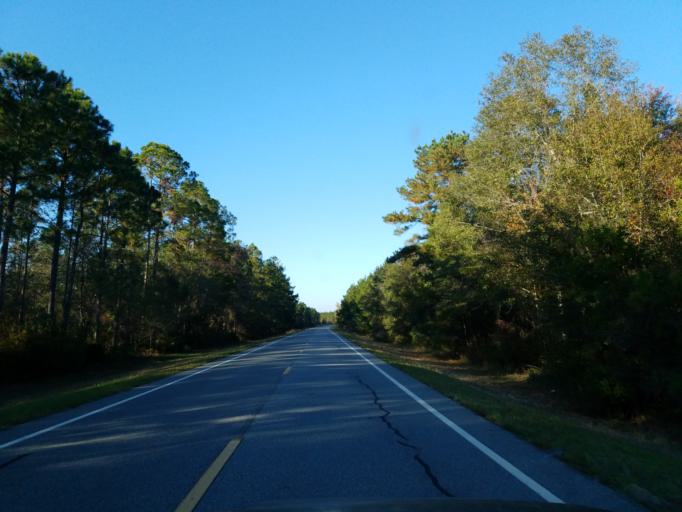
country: US
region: Georgia
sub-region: Lanier County
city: Lakeland
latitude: 30.8795
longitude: -83.0529
